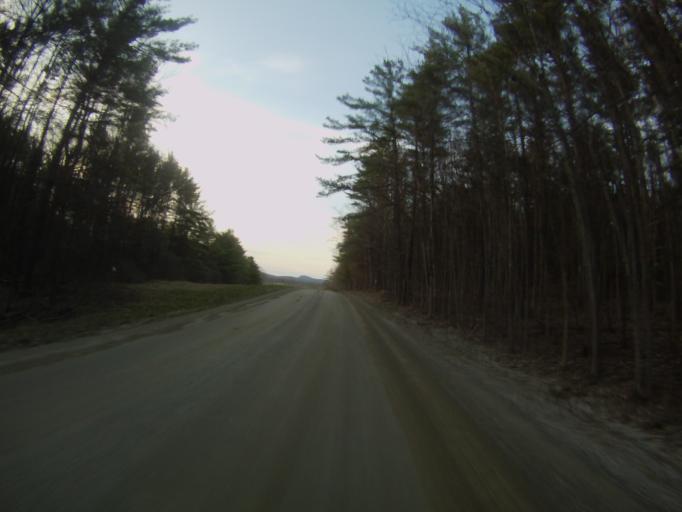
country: US
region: Vermont
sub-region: Addison County
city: Middlebury (village)
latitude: 44.0268
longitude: -73.2206
